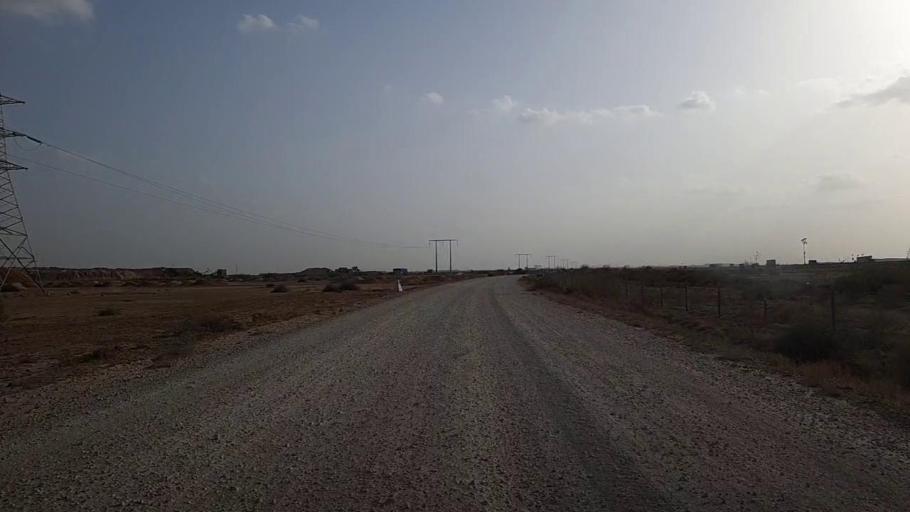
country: PK
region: Sindh
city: Thatta
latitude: 25.1990
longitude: 67.8796
